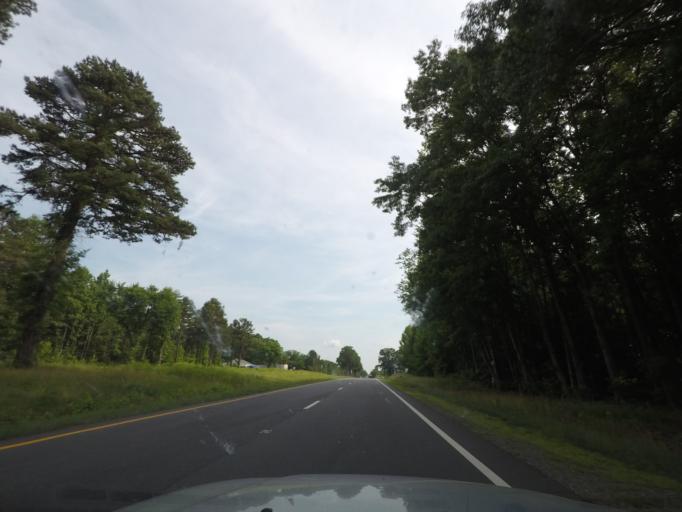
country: US
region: Virginia
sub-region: Mecklenburg County
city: Chase City
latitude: 36.9576
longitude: -78.4970
